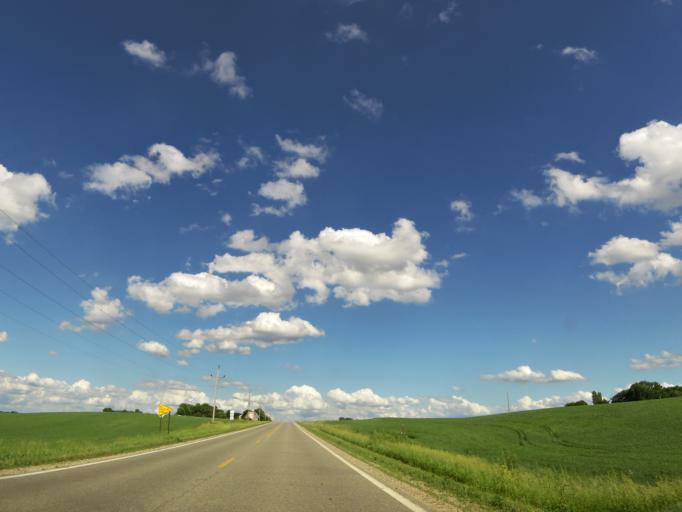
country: US
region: Minnesota
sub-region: Meeker County
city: Dassel
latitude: 45.0663
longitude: -94.2745
